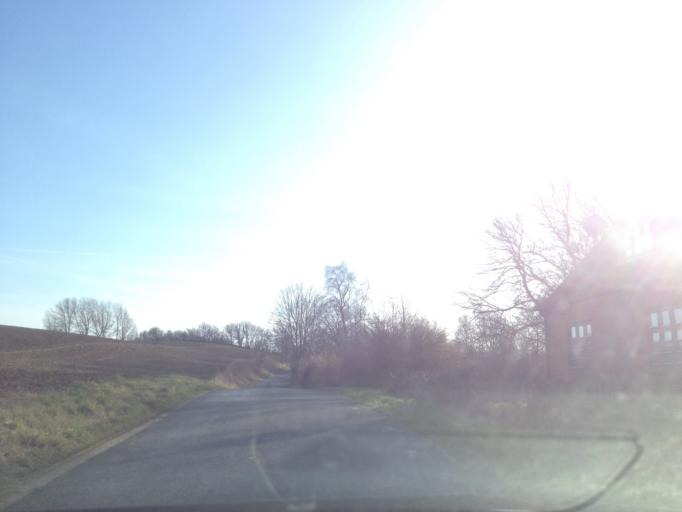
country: DK
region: South Denmark
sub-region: Kerteminde Kommune
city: Munkebo
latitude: 55.5637
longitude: 10.6142
